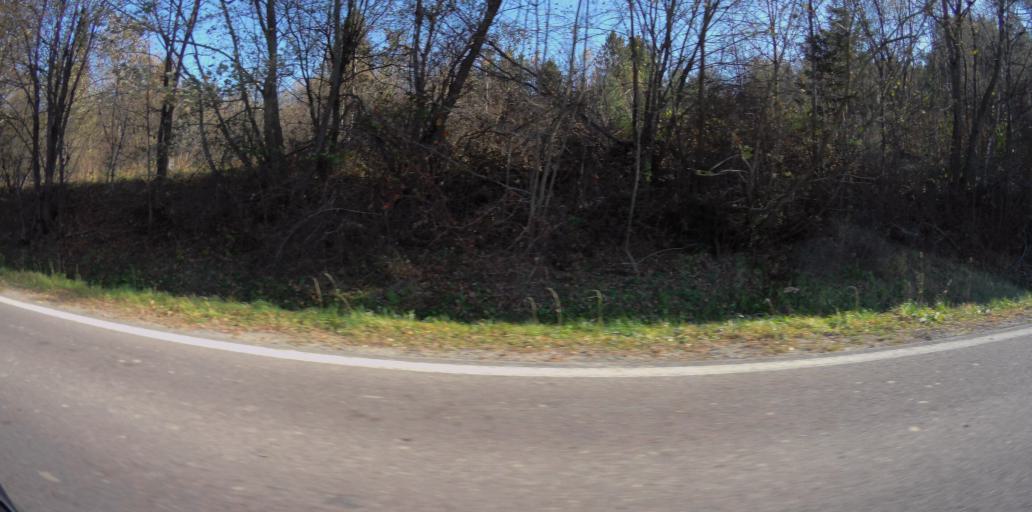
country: PL
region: Subcarpathian Voivodeship
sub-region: Powiat bieszczadzki
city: Ustrzyki Dolne
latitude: 49.5256
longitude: 22.6043
